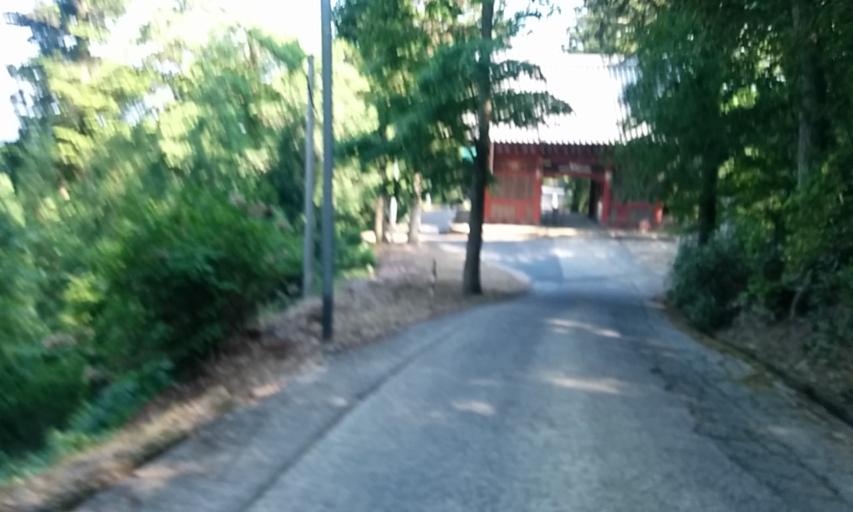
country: JP
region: Kyoto
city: Miyazu
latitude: 35.5932
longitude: 135.1880
